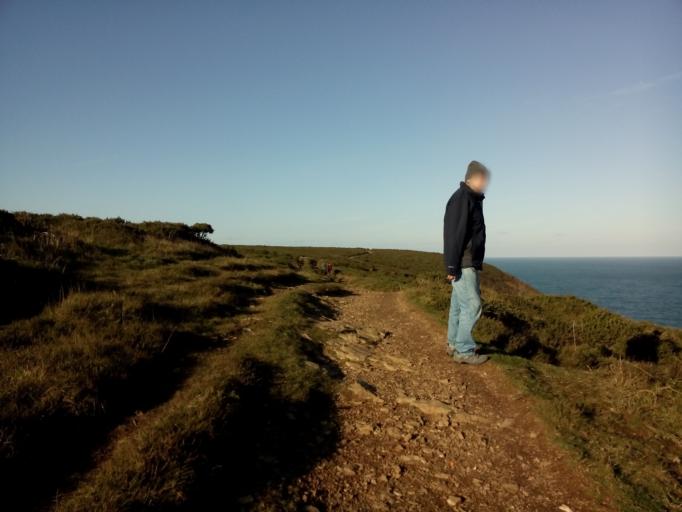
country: GB
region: England
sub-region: Cornwall
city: Hayle
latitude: 50.2390
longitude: -5.3761
